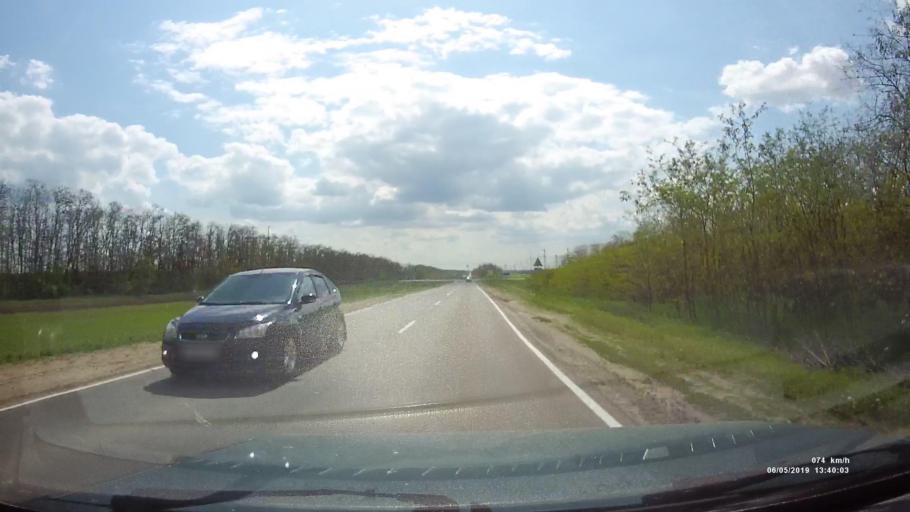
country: RU
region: Rostov
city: Ust'-Donetskiy
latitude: 47.6691
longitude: 40.6976
